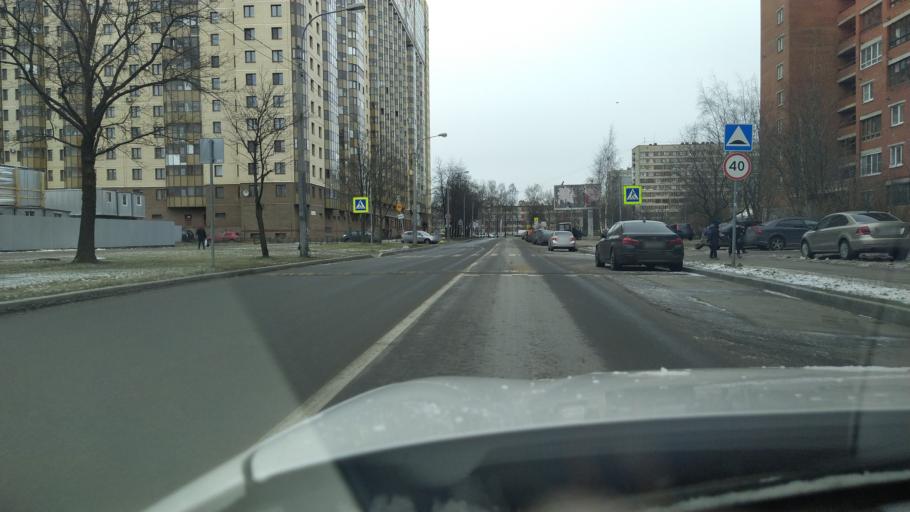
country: RU
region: Leningrad
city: Akademicheskoe
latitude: 60.0090
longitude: 30.4039
